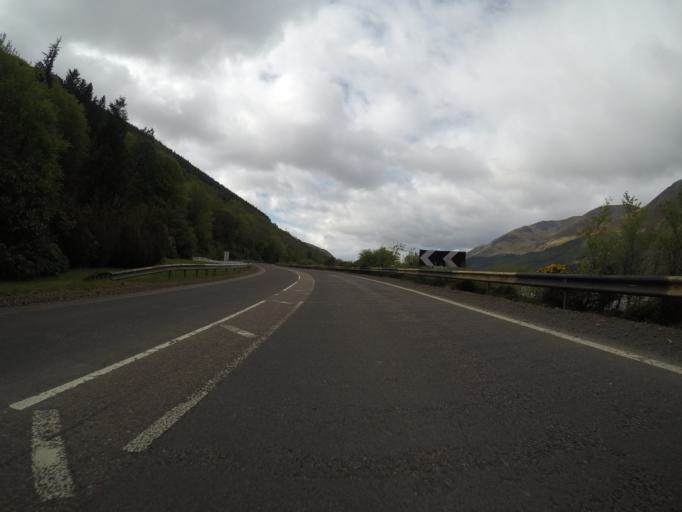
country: GB
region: Scotland
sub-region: Highland
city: Spean Bridge
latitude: 56.9925
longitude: -4.8639
